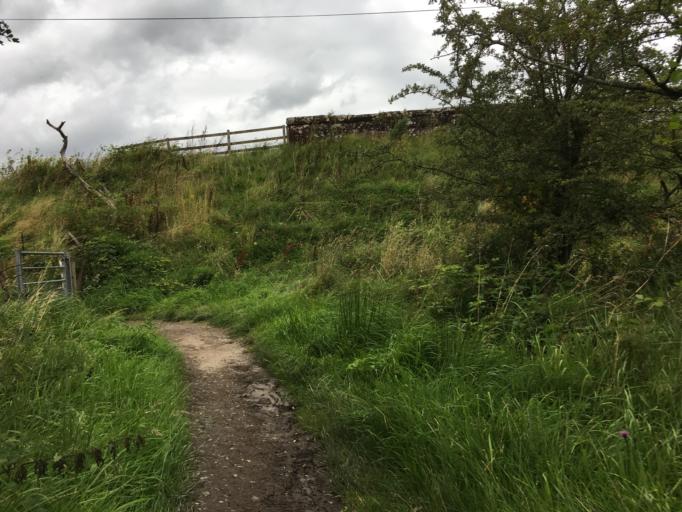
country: GB
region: Scotland
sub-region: Stirling
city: Killearn
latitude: 56.0518
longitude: -4.4041
